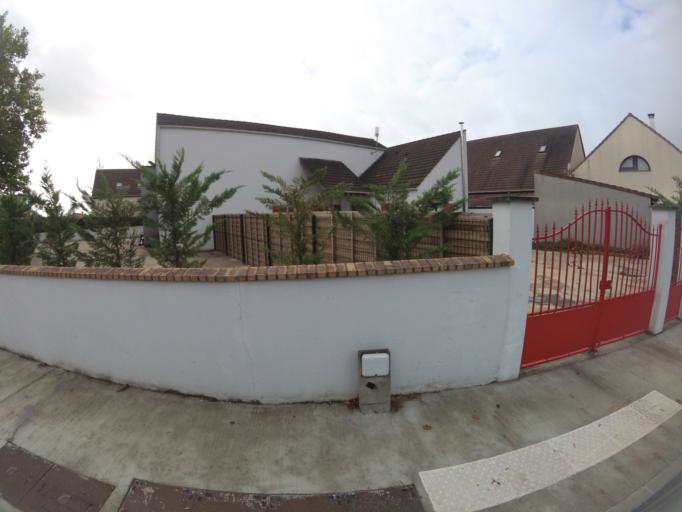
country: FR
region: Ile-de-France
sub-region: Departement de Seine-et-Marne
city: Montevrain
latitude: 48.8752
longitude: 2.7522
